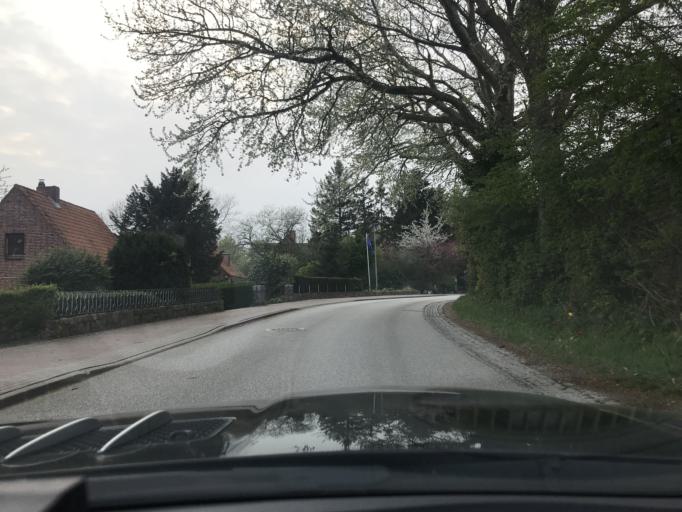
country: DE
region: Schleswig-Holstein
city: Burg auf Fehmarn
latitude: 54.4230
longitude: 11.2530
